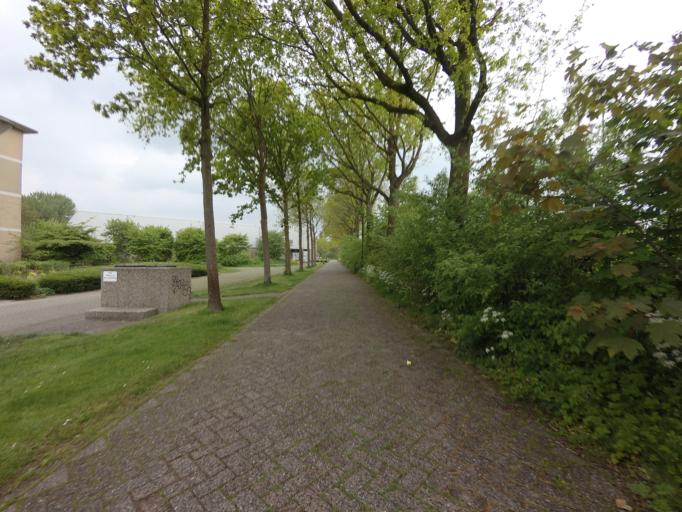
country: NL
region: Utrecht
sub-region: Gemeente IJsselstein
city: IJsselstein
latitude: 52.0239
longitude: 5.0565
